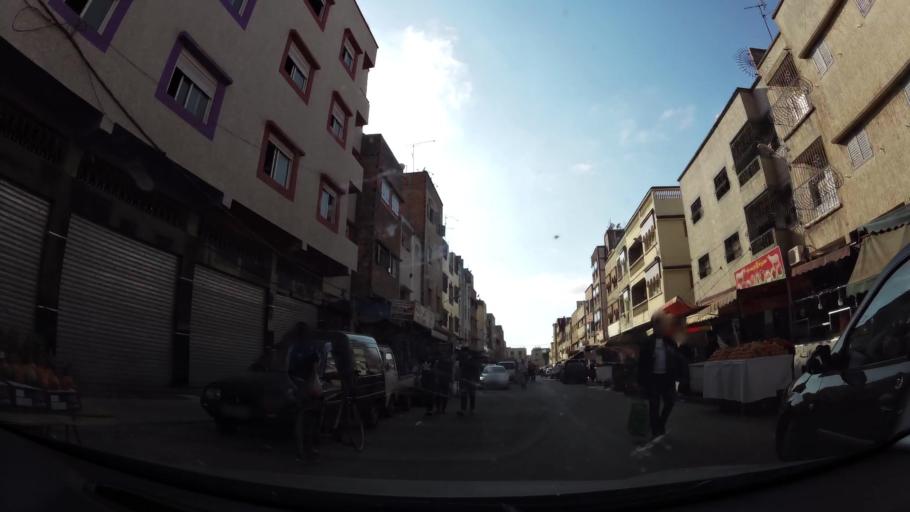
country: MA
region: Rabat-Sale-Zemmour-Zaer
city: Sale
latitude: 34.0520
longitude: -6.7790
